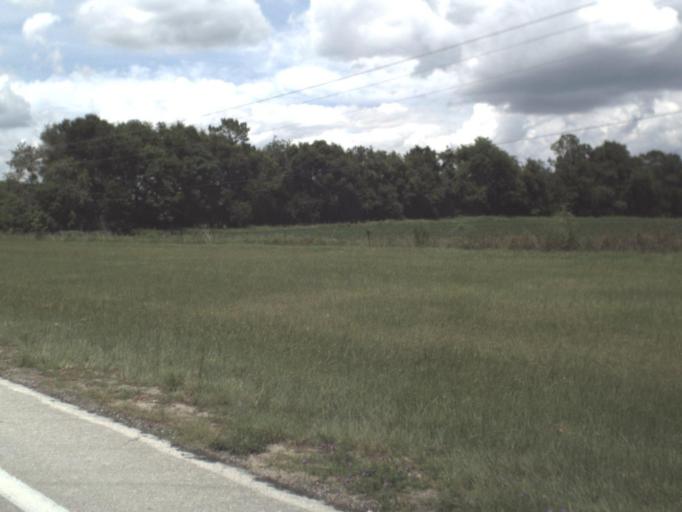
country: US
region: Florida
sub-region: Alachua County
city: Newberry
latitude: 29.7008
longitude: -82.6070
